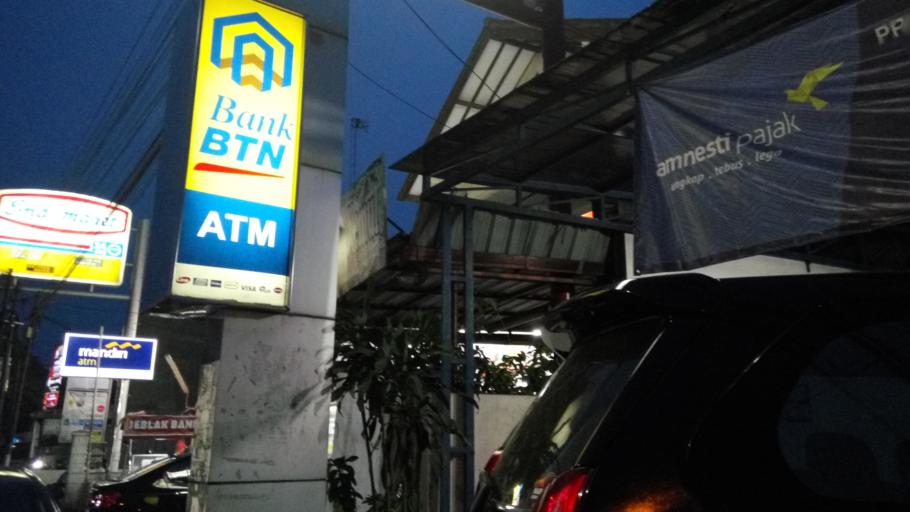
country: ID
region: Central Java
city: Semarang
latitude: -7.0561
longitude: 110.4388
